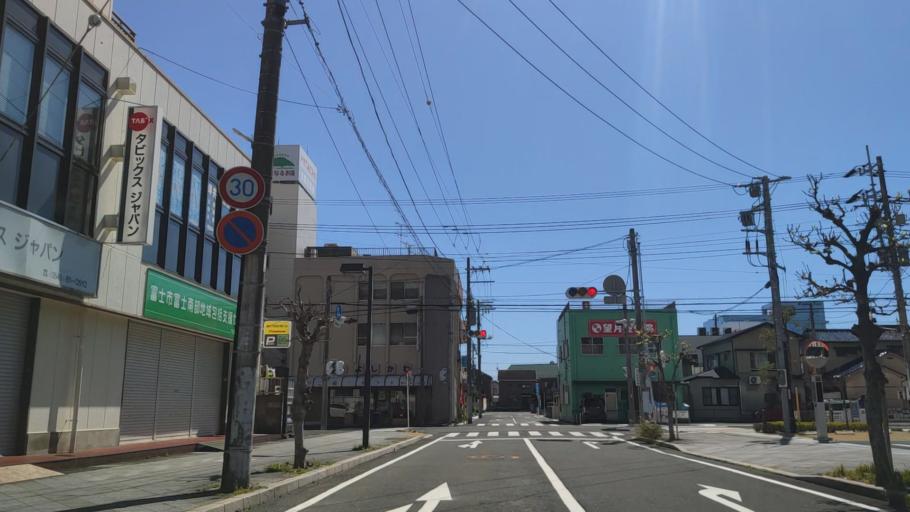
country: JP
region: Shizuoka
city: Fuji
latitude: 35.1506
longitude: 138.6516
